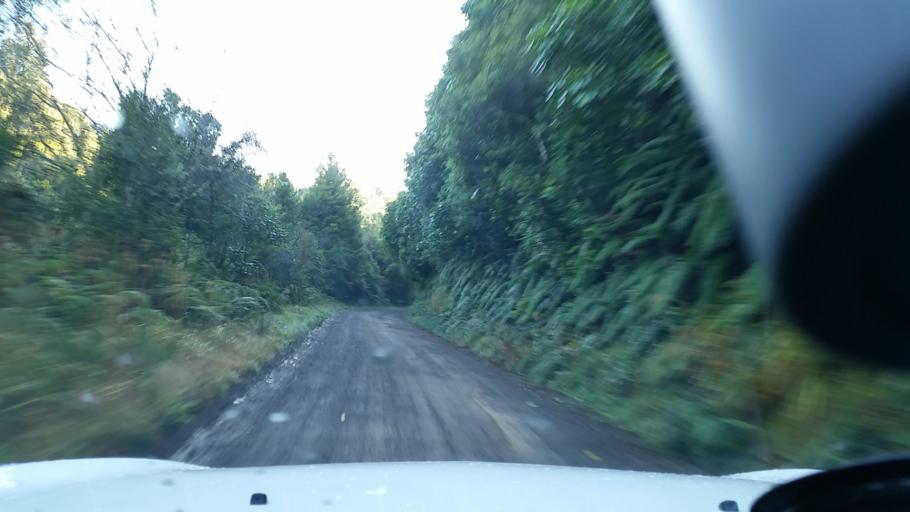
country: NZ
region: Bay of Plenty
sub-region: Kawerau District
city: Kawerau
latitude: -38.0061
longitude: 176.5984
